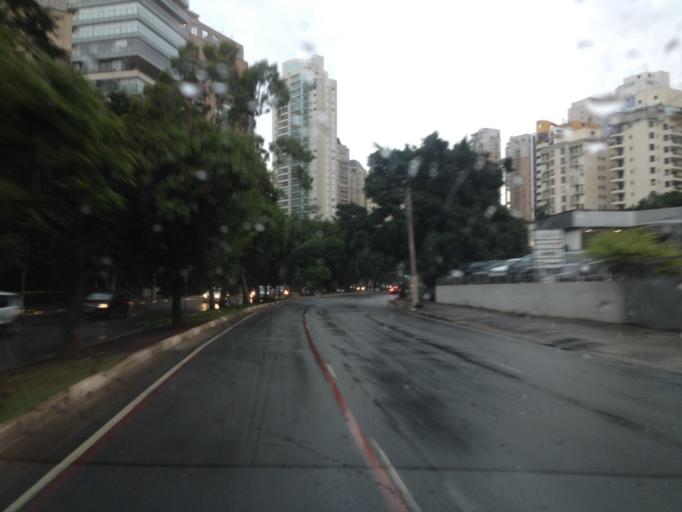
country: BR
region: Sao Paulo
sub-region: Sao Paulo
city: Sao Paulo
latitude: -23.5979
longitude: -46.6698
